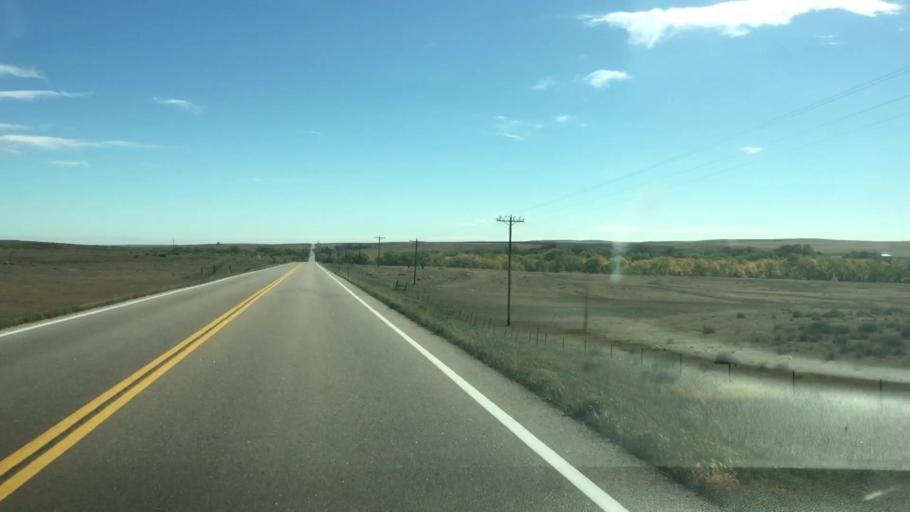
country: US
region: Colorado
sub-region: Elbert County
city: Kiowa
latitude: 39.2736
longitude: -104.1529
